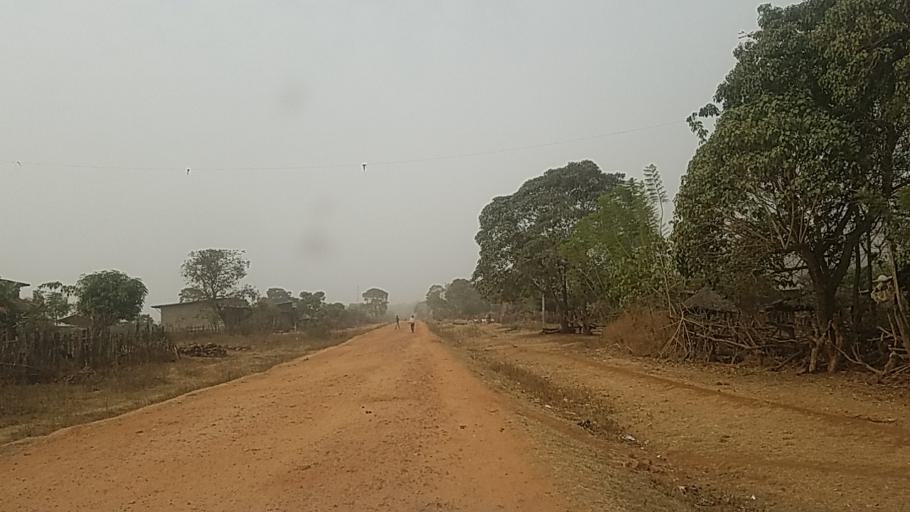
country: ET
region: Amhara
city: Bure
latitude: 10.8618
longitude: 36.3893
